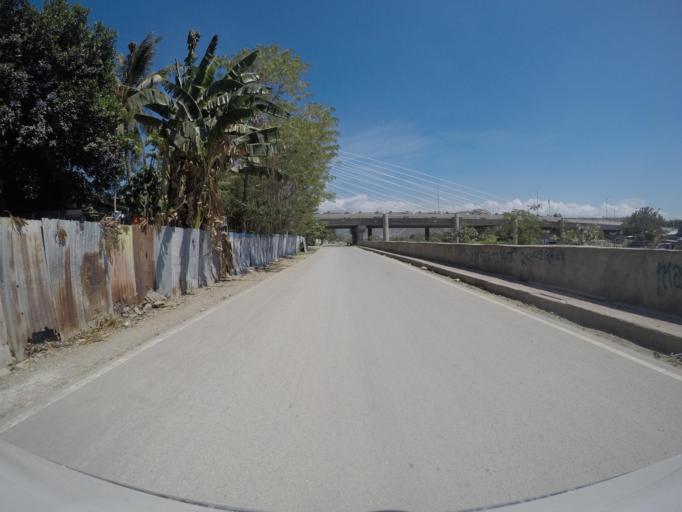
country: TL
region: Dili
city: Dili
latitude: -8.5535
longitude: 125.5369
